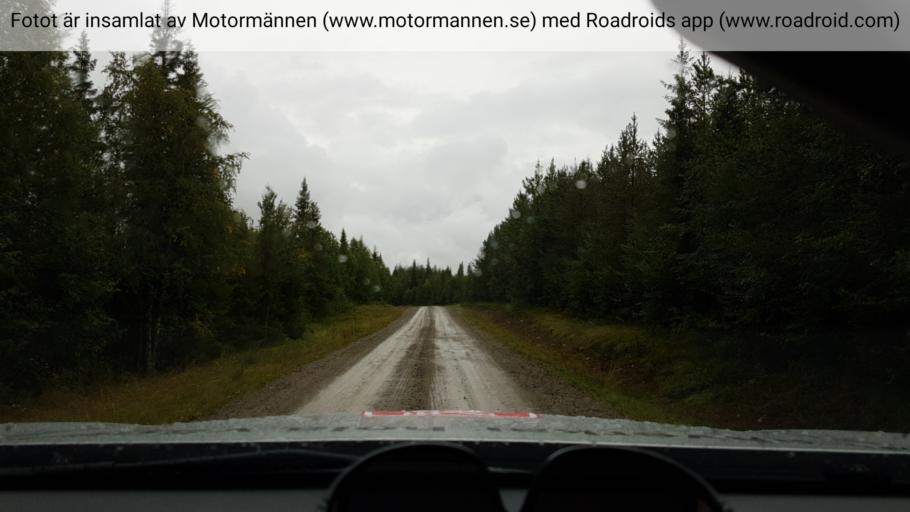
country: SE
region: Vaesterbotten
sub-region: Asele Kommun
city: Insjon
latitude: 64.7907
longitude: 17.5086
